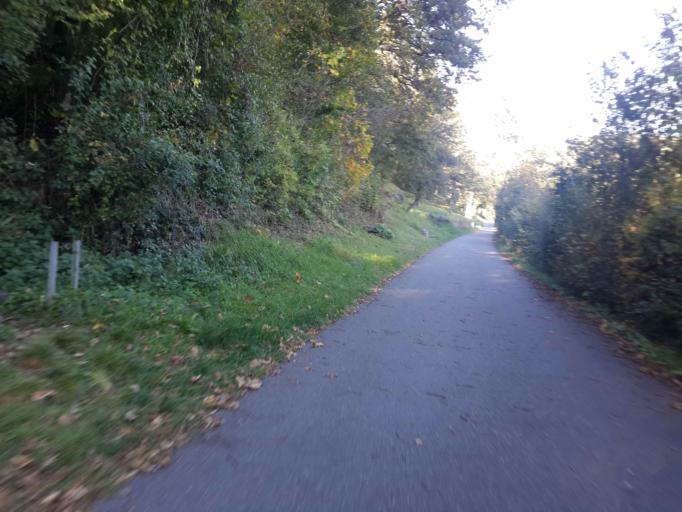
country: DE
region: Baden-Wuerttemberg
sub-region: Regierungsbezirk Stuttgart
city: Wertheim
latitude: 49.7495
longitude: 9.5111
